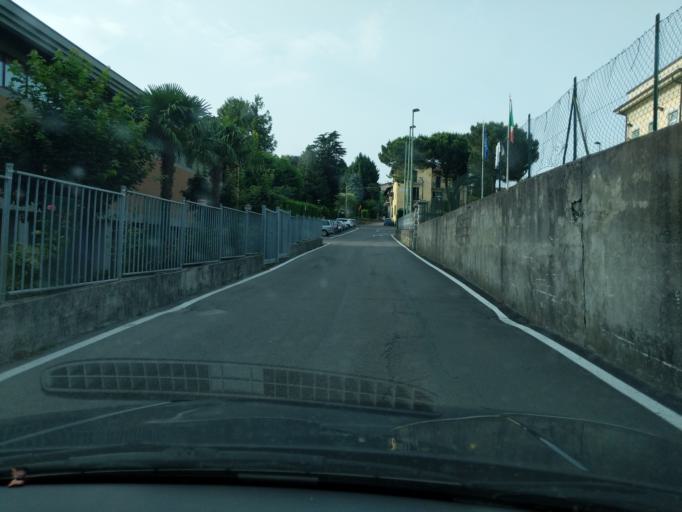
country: IT
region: Lombardy
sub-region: Provincia di Como
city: Bellagio
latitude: 45.9769
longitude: 9.2600
